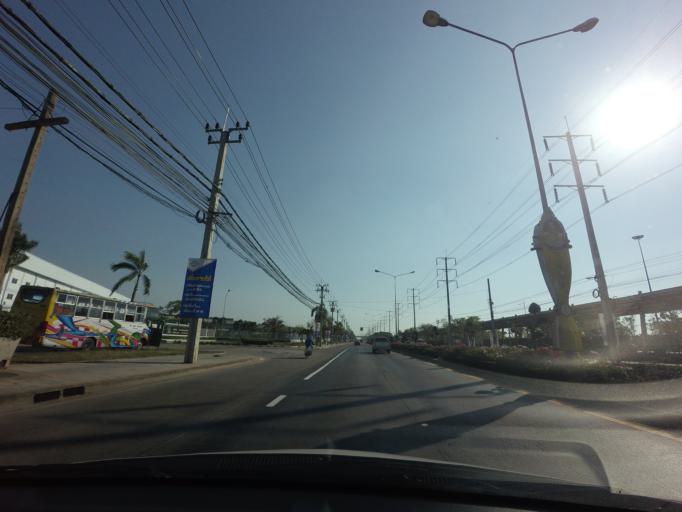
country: TH
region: Bangkok
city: Nong Chok
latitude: 13.8320
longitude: 100.8508
